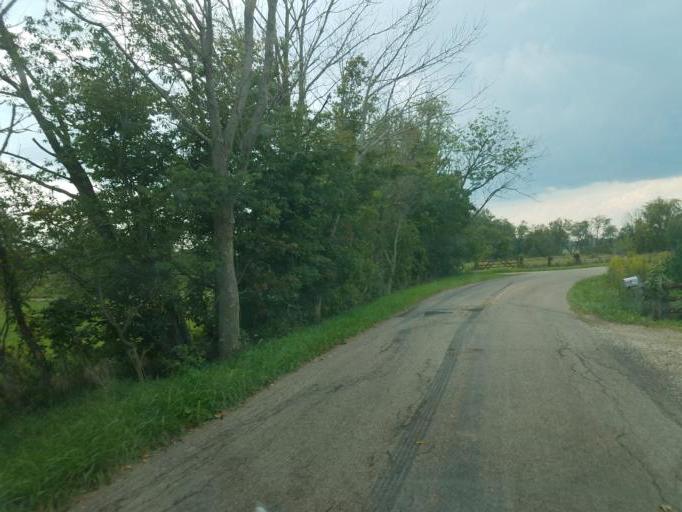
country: US
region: Ohio
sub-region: Knox County
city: Gambier
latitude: 40.3638
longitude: -82.3169
